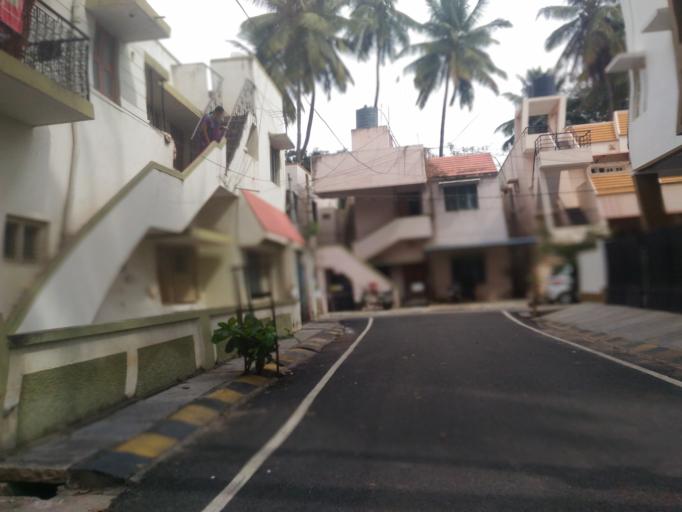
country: IN
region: Karnataka
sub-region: Bangalore Urban
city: Bangalore
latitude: 12.9309
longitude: 77.5914
